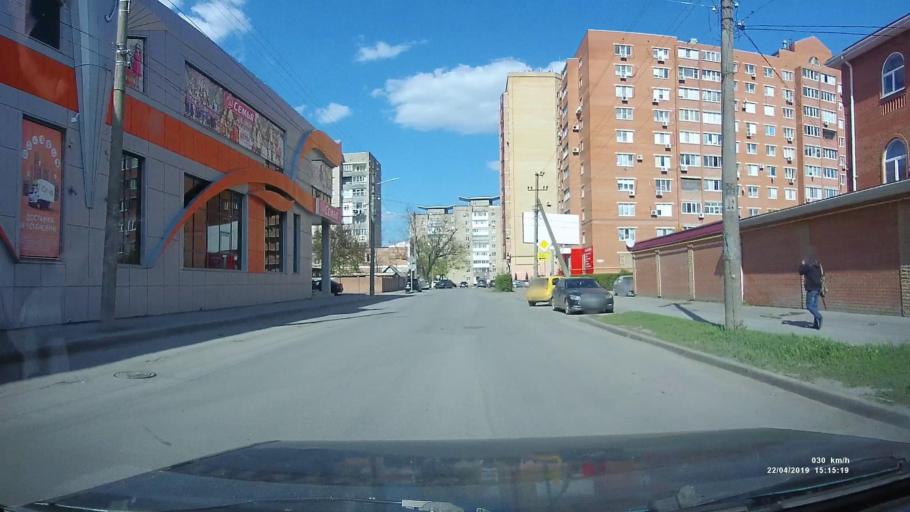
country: RU
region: Rostov
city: Azov
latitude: 47.1064
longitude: 39.4287
